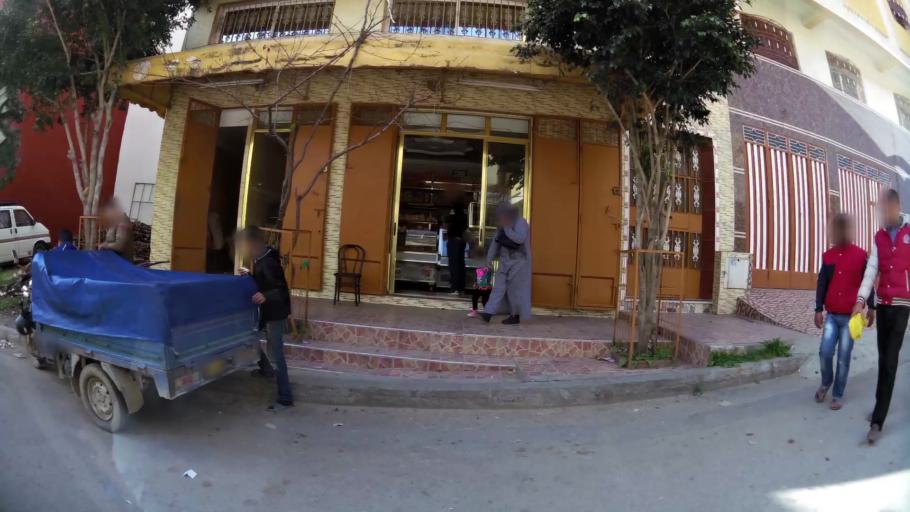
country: MA
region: Tanger-Tetouan
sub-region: Tanger-Assilah
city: Tangier
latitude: 35.7269
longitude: -5.8071
